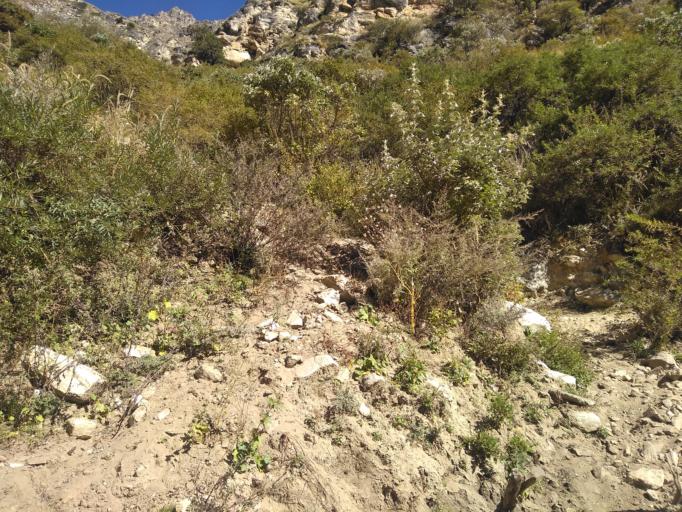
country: NP
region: Western Region
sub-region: Dhawalagiri Zone
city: Jomsom
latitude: 28.9343
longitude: 83.0473
